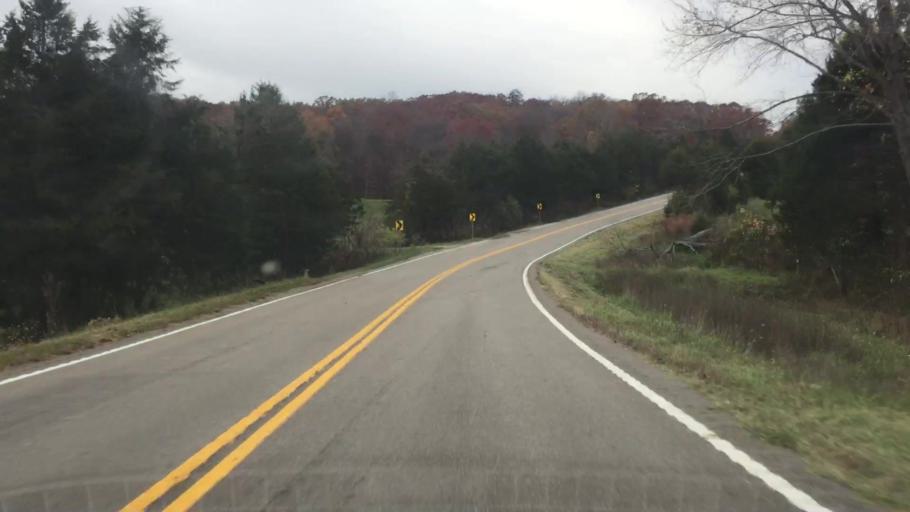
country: US
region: Missouri
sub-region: Gasconade County
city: Hermann
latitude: 38.7178
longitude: -91.6645
